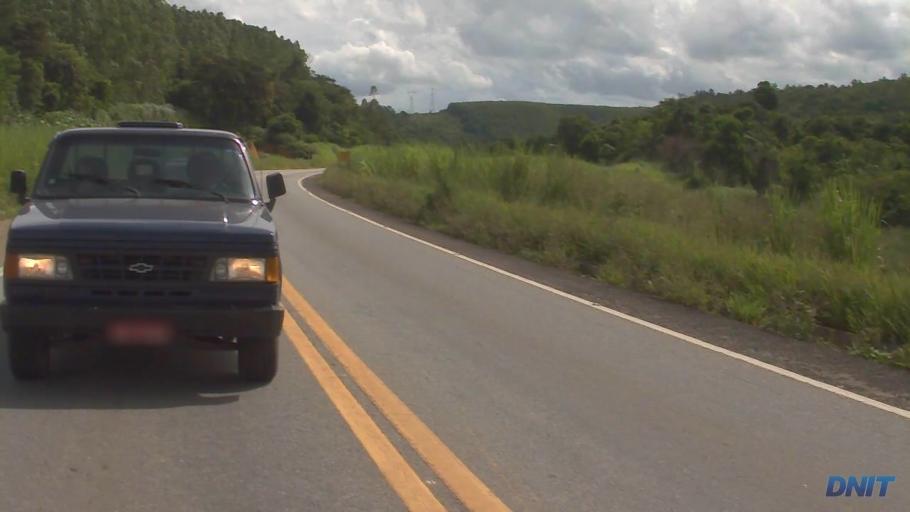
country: BR
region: Minas Gerais
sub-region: Ipaba
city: Ipaba
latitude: -19.3931
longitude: -42.4822
